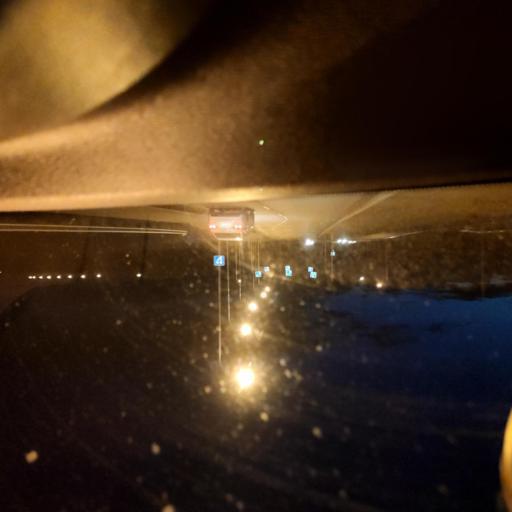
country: RU
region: Samara
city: Petra-Dubrava
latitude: 53.3010
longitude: 50.3151
